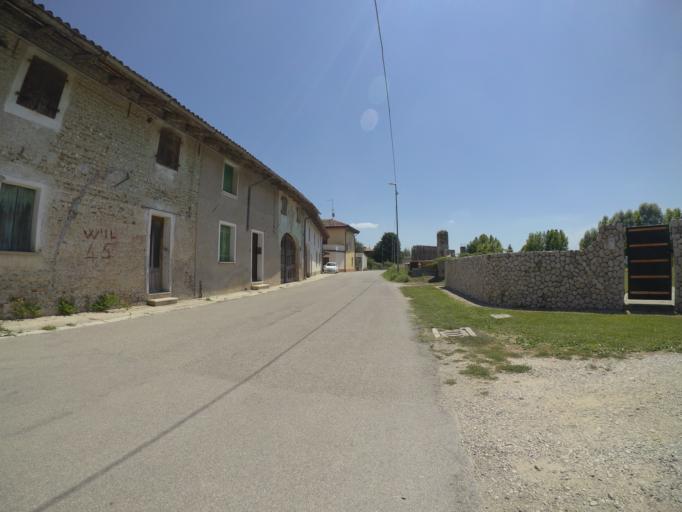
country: IT
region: Friuli Venezia Giulia
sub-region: Provincia di Udine
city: Varmo
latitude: 45.8928
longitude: 13.0039
